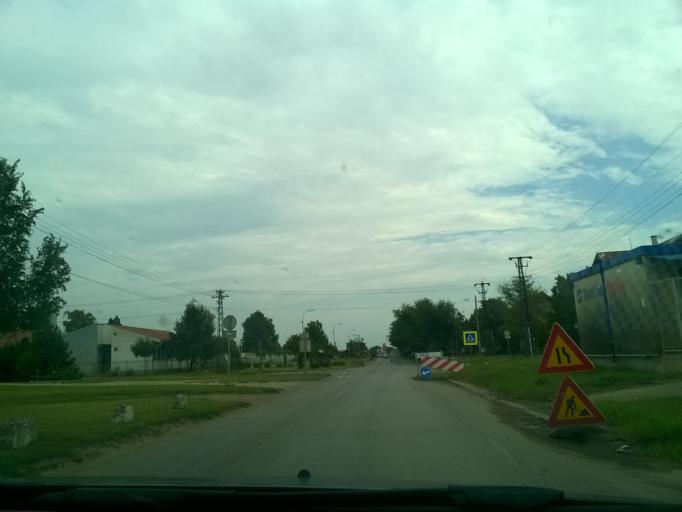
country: RS
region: Autonomna Pokrajina Vojvodina
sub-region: Srednjebanatski Okrug
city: Zrenjanin
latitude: 45.3958
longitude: 20.4010
